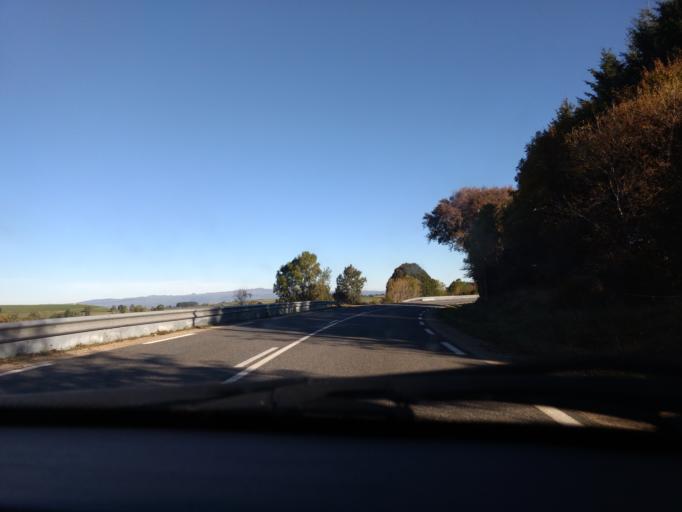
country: FR
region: Midi-Pyrenees
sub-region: Departement de l'Aveyron
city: Laguiole
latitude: 44.7492
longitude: 2.8705
